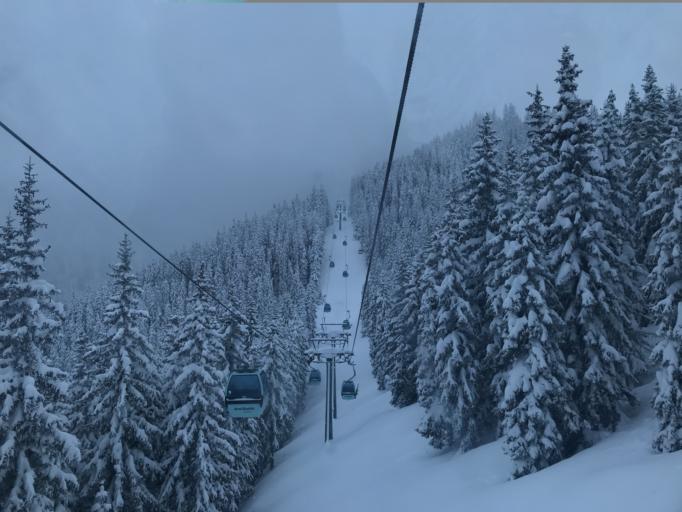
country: AT
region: Salzburg
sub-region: Politischer Bezirk Zell am See
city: Piesendorf
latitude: 47.3176
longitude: 12.7467
